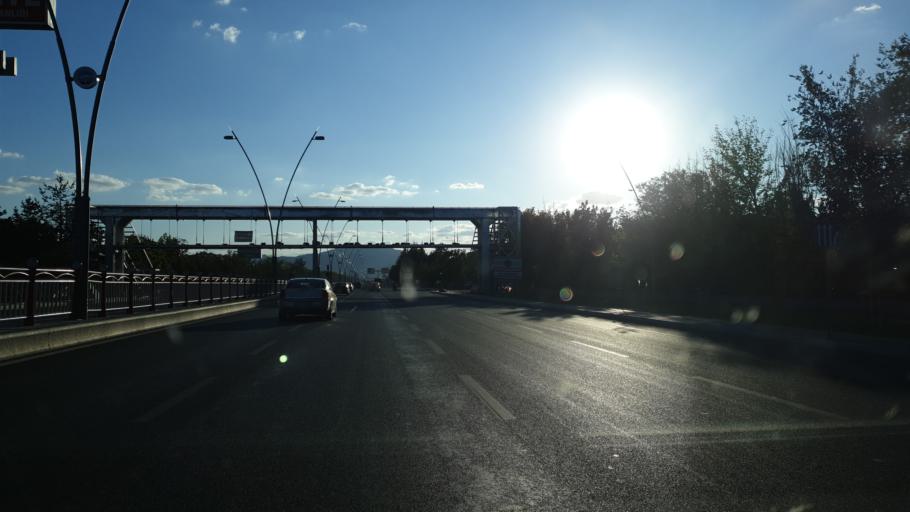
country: TR
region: Kayseri
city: Kayseri
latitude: 38.7390
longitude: 35.5099
